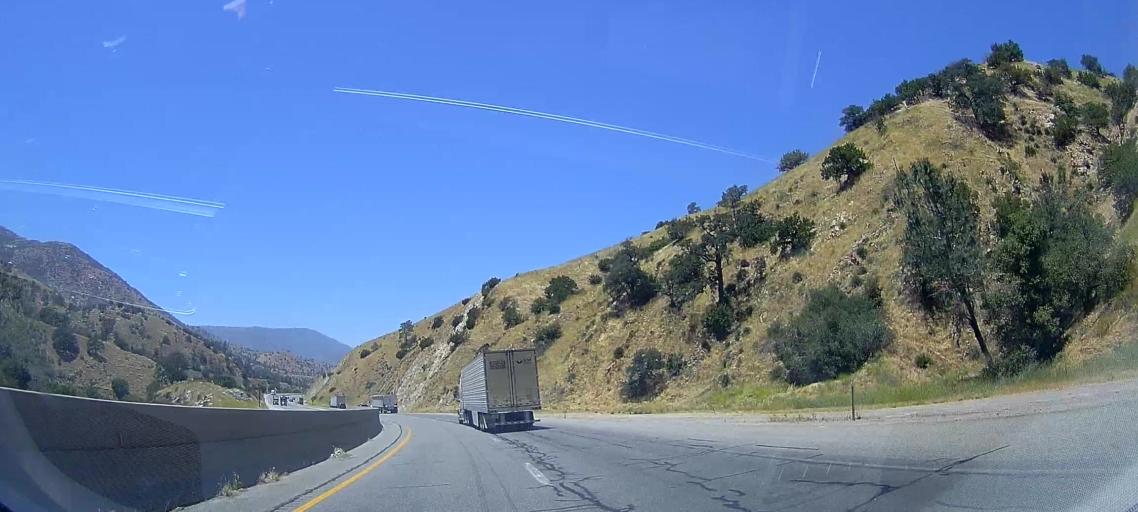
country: US
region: California
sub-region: Kern County
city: Golden Hills
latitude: 35.1812
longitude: -118.4891
